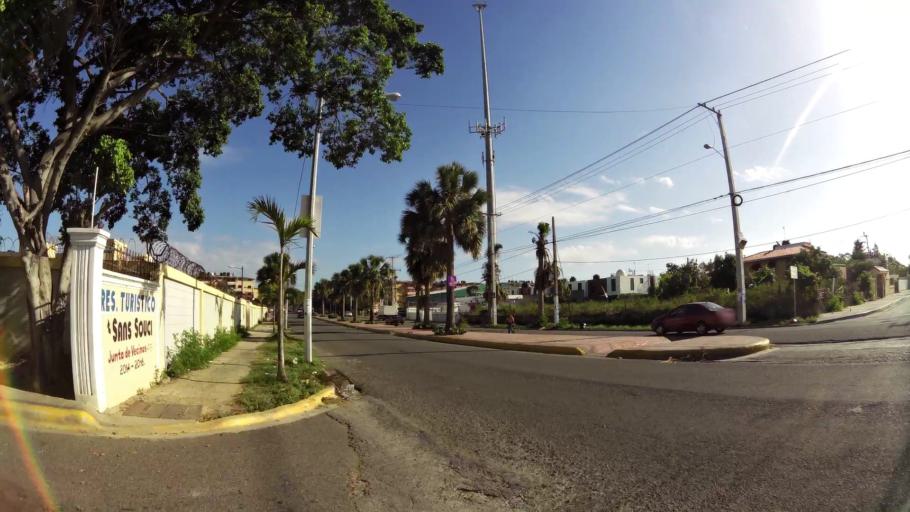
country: DO
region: Santo Domingo
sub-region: Santo Domingo
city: Santo Domingo Este
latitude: 18.4712
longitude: -69.8560
